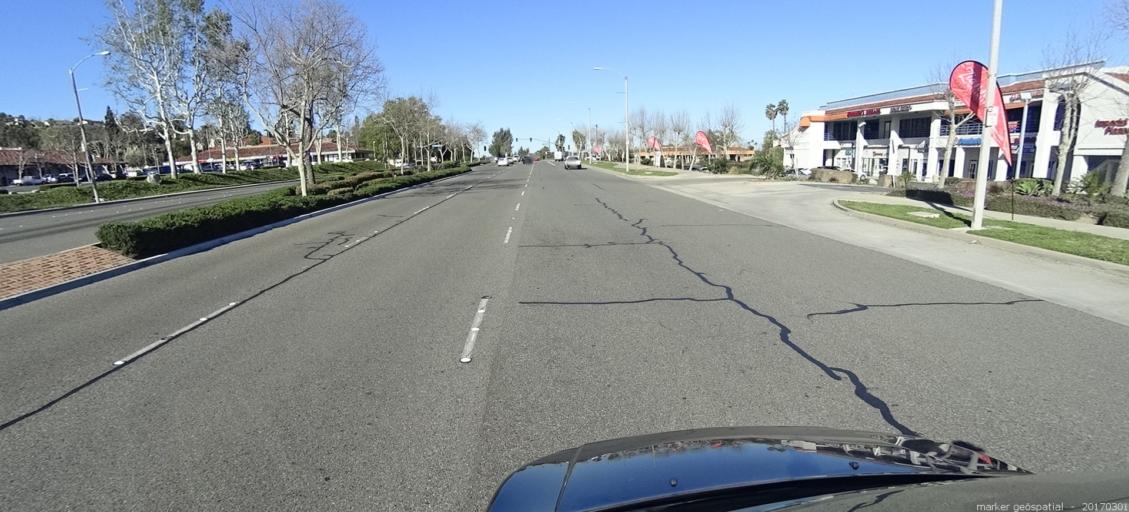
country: US
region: California
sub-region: Orange County
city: Villa Park
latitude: 33.8515
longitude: -117.7914
